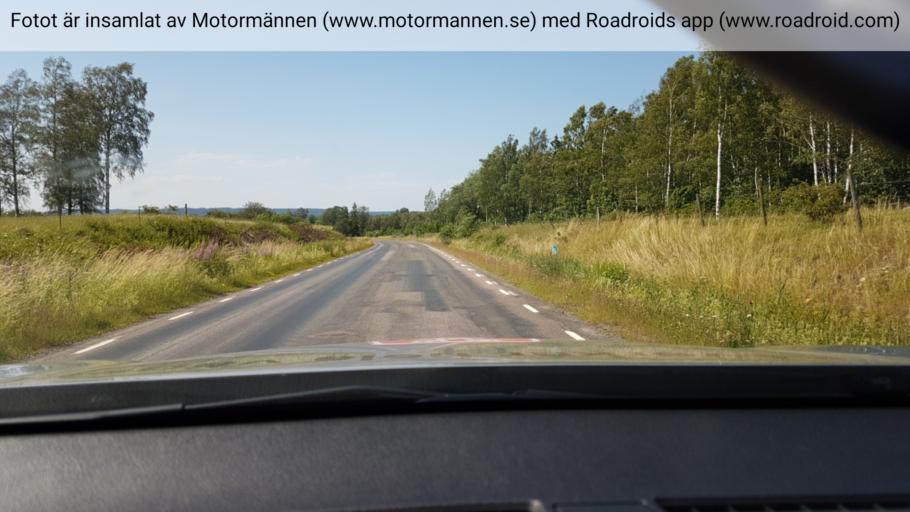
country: SE
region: Vaestra Goetaland
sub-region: Skovde Kommun
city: Skultorp
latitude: 58.2605
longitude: 13.7720
